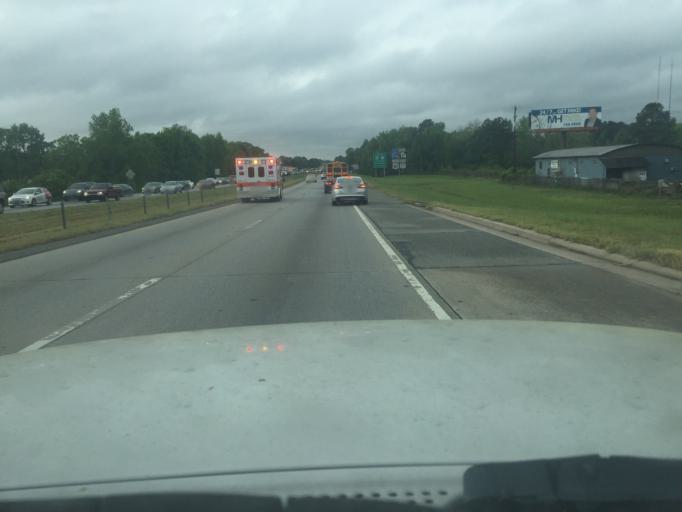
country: US
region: Georgia
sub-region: Chatham County
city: Savannah
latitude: 32.0643
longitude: -81.1379
